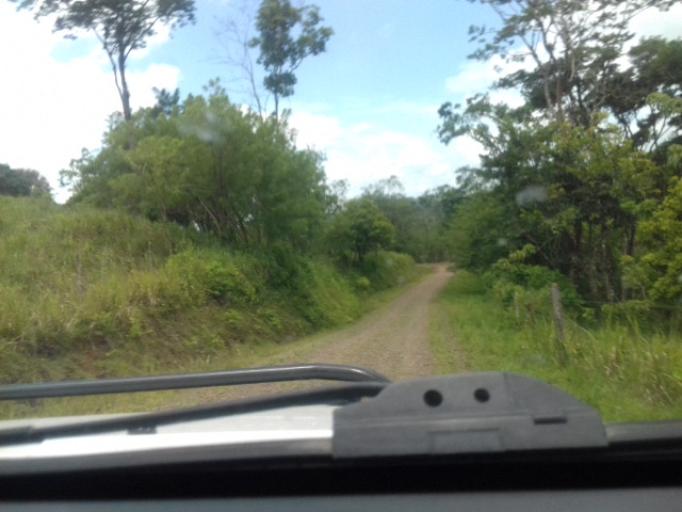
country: NI
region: Matagalpa
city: Matiguas
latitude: 13.0223
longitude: -85.4075
